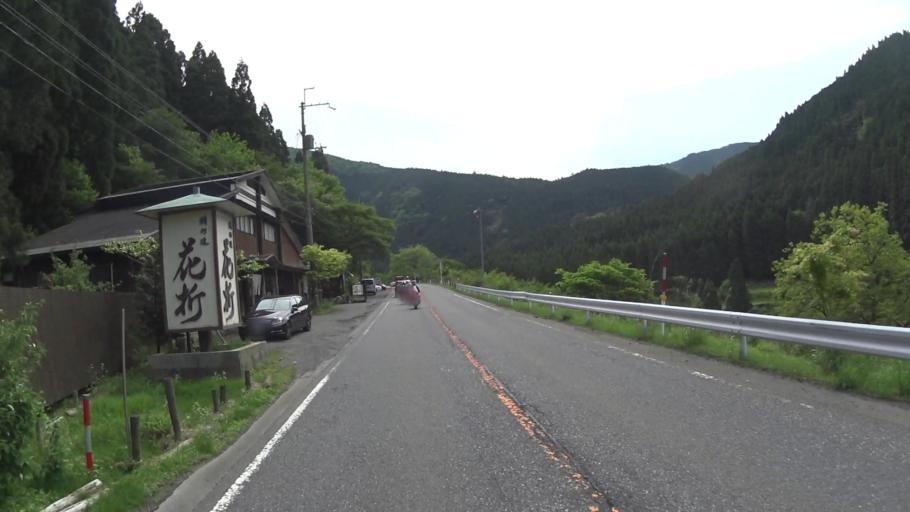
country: JP
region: Shiga Prefecture
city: Kitahama
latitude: 35.1913
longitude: 135.8583
